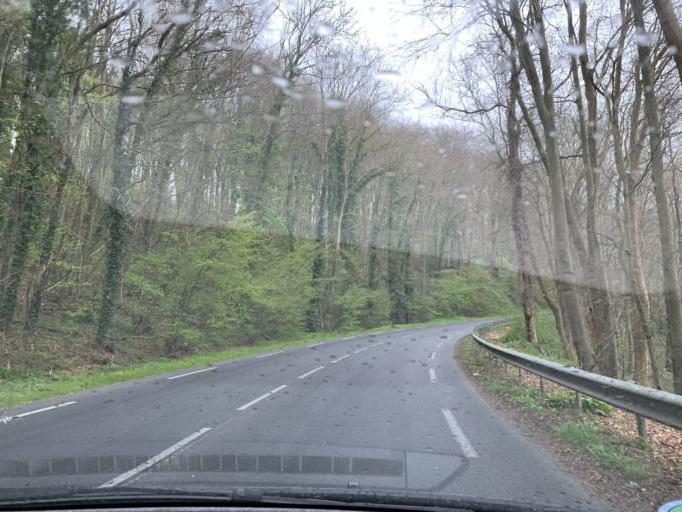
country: FR
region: Haute-Normandie
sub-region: Departement de la Seine-Maritime
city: Cany-Barville
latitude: 49.7877
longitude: 0.6460
